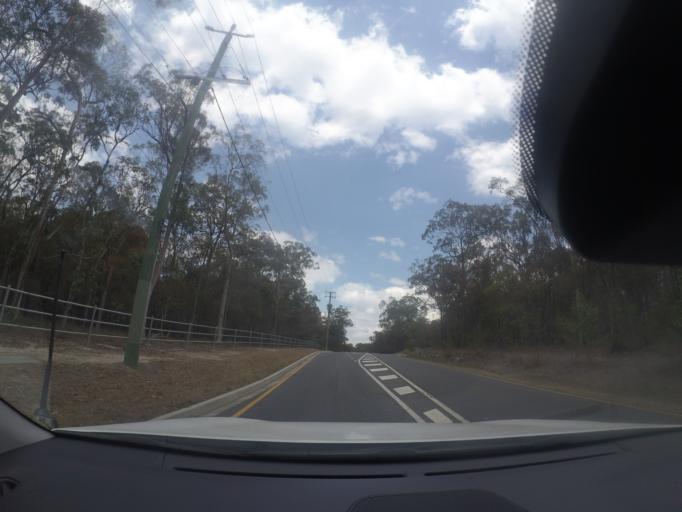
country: AU
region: Queensland
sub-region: Logan
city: Woodridge
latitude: -27.6226
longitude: 153.0941
